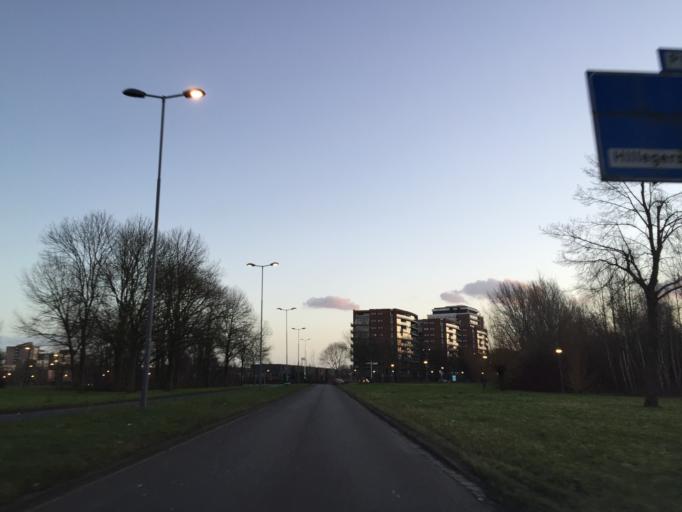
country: NL
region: South Holland
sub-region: Gemeente Lansingerland
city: Bergschenhoek
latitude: 51.9686
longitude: 4.4863
